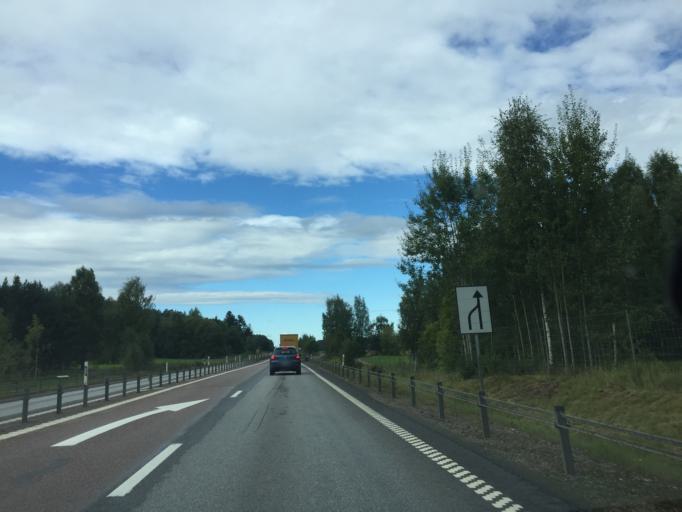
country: SE
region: Vaestmanland
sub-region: Kungsors Kommun
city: Kungsoer
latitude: 59.4107
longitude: 16.0861
